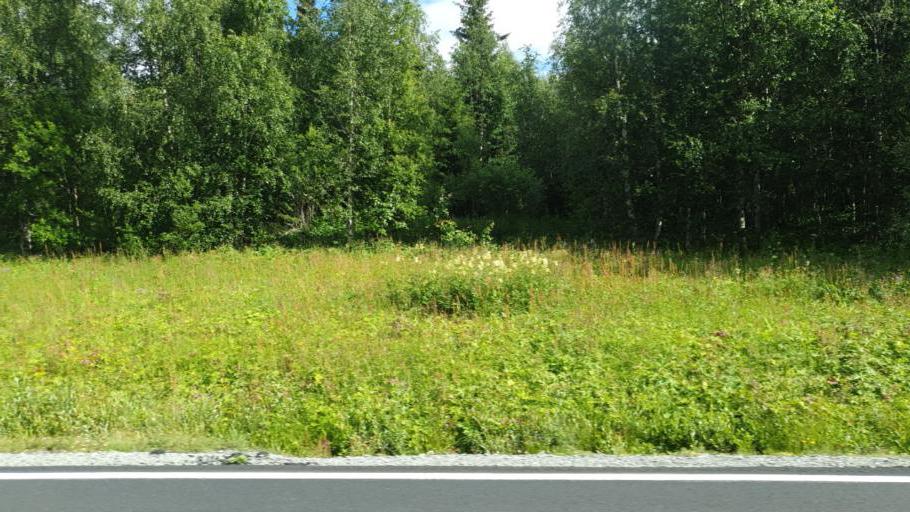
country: NO
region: Oppland
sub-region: Oystre Slidre
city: Heggenes
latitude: 61.1803
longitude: 9.0000
